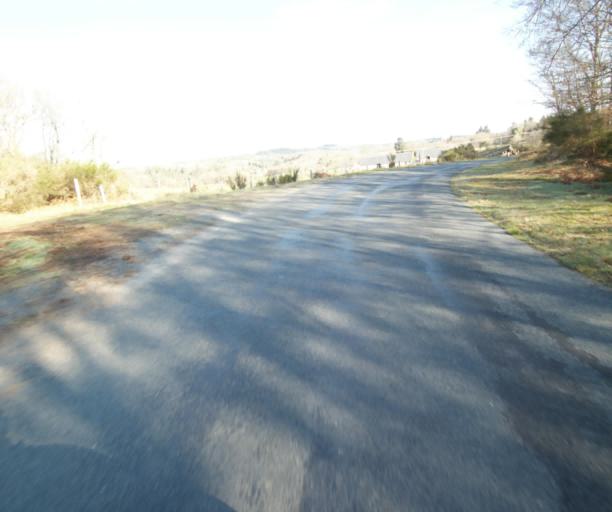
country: FR
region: Limousin
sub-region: Departement de la Correze
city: Correze
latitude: 45.2979
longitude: 1.8693
